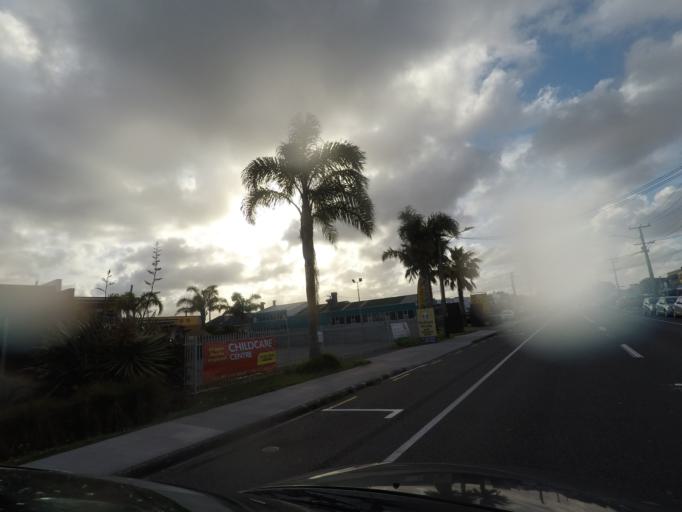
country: NZ
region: Auckland
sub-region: Auckland
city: Auckland
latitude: -36.9135
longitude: 174.7522
